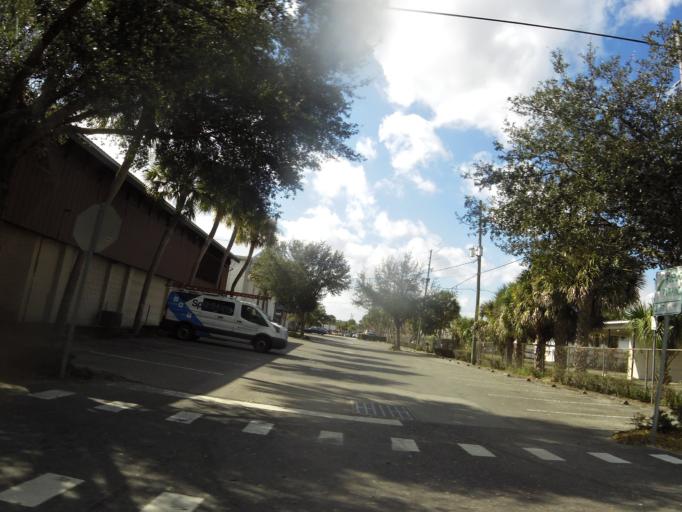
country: US
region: Florida
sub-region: Volusia County
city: DeLand
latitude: 29.0272
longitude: -81.3014
